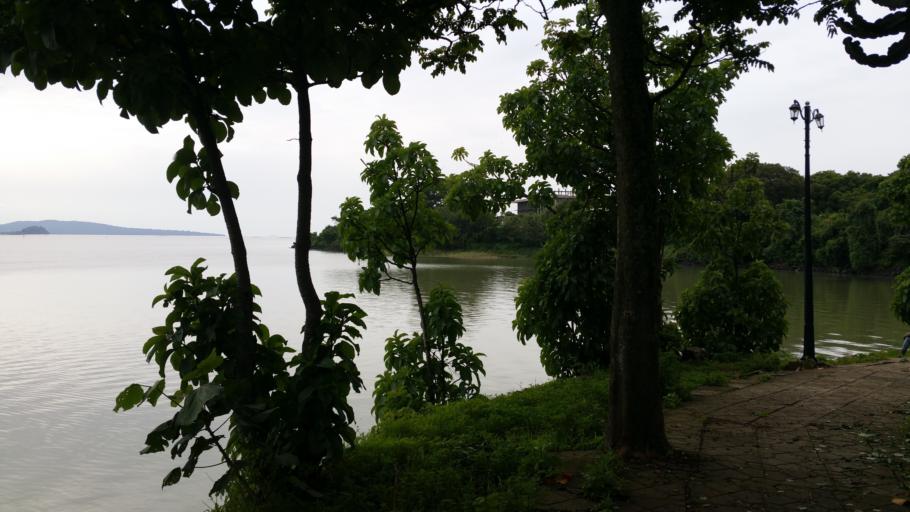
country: ET
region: Amhara
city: Bahir Dar
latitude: 11.6042
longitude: 37.3939
